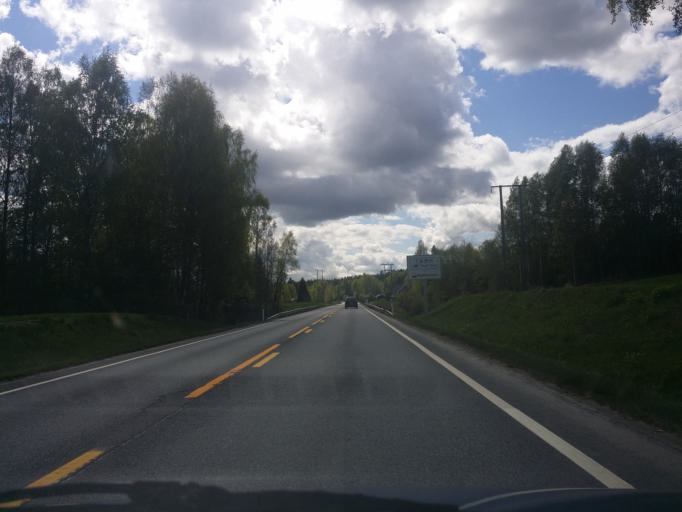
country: NO
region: Buskerud
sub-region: Modum
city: Vikersund
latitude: 59.9498
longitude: 9.9717
